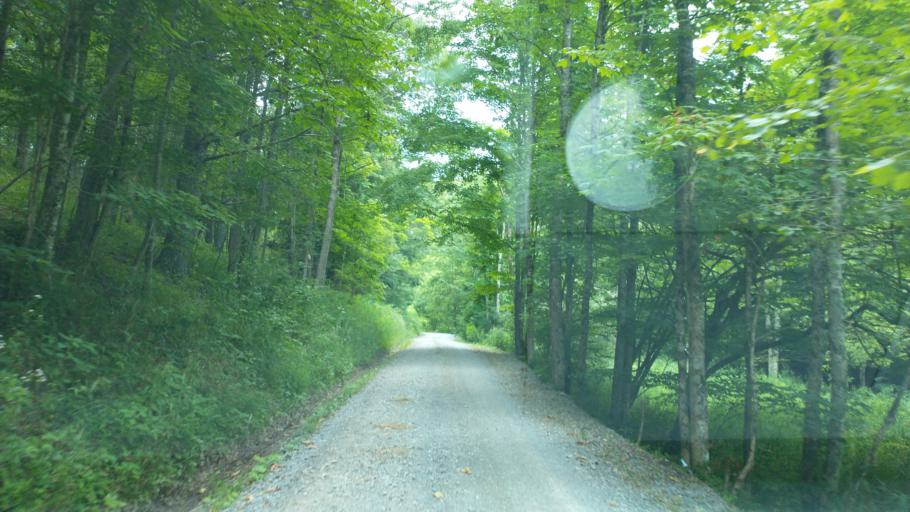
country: US
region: West Virginia
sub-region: Mercer County
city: Athens
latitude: 37.4353
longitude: -81.0006
